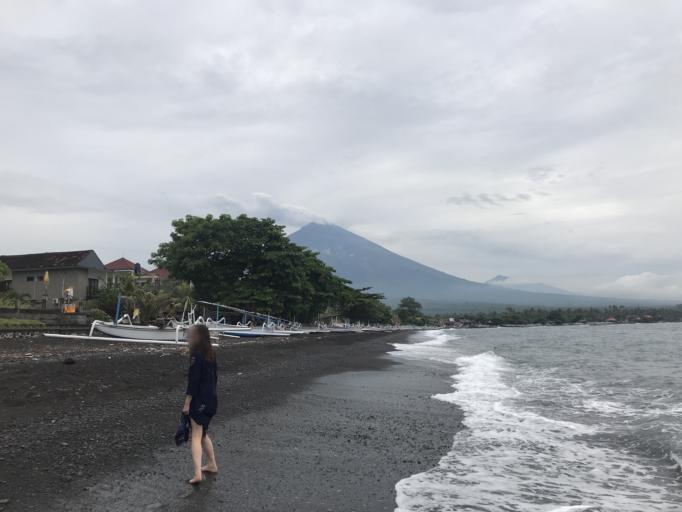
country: ID
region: Bali
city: Biaslantang Kaler
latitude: -8.3343
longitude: 115.6456
